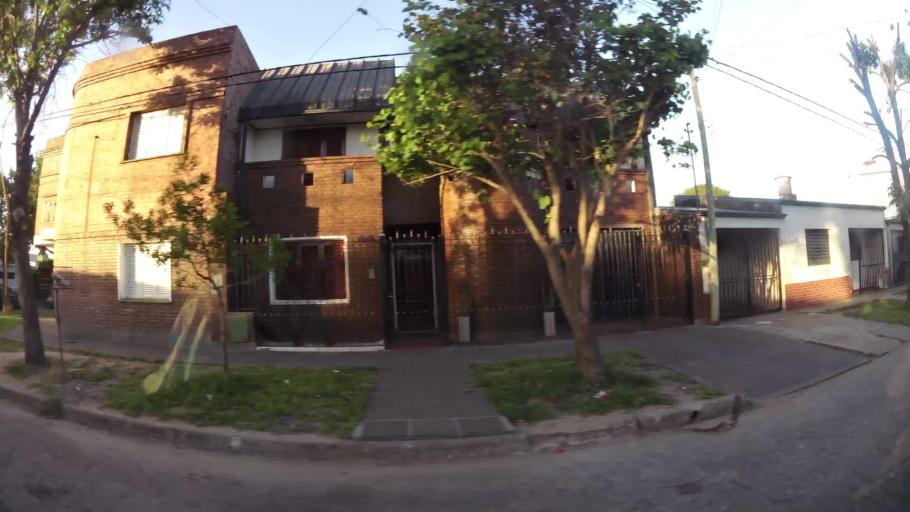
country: AR
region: Santa Fe
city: Santa Fe de la Vera Cruz
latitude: -31.6008
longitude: -60.6891
